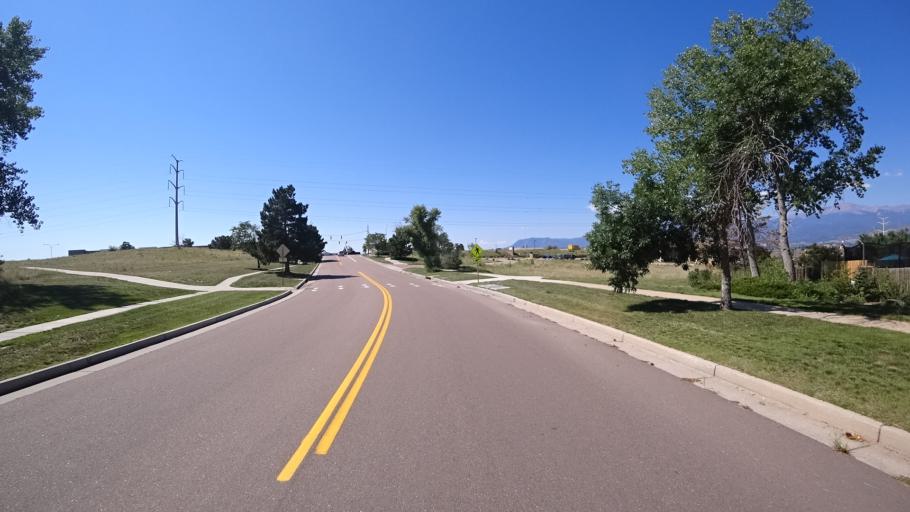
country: US
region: Colorado
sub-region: El Paso County
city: Black Forest
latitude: 38.9415
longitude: -104.7483
